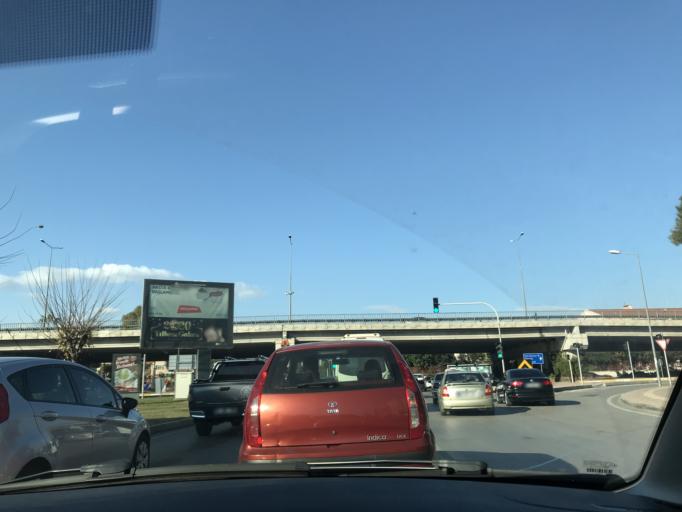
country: TR
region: Antalya
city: Antalya
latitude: 36.9102
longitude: 30.6983
